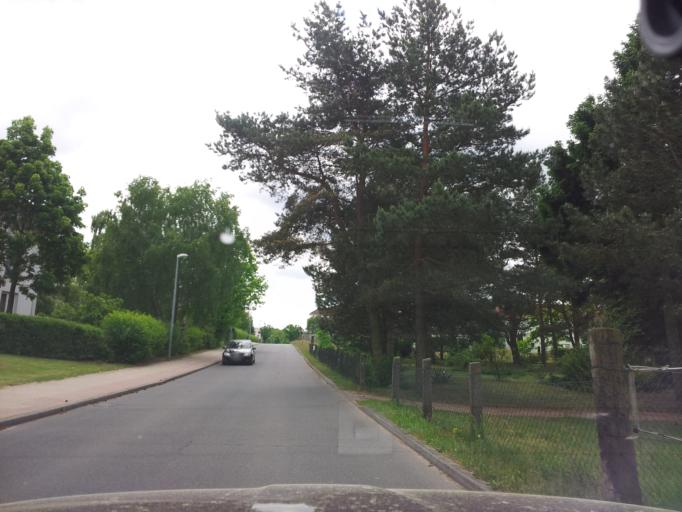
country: DE
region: Brandenburg
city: Treuenbrietzen
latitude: 52.0901
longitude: 12.8474
